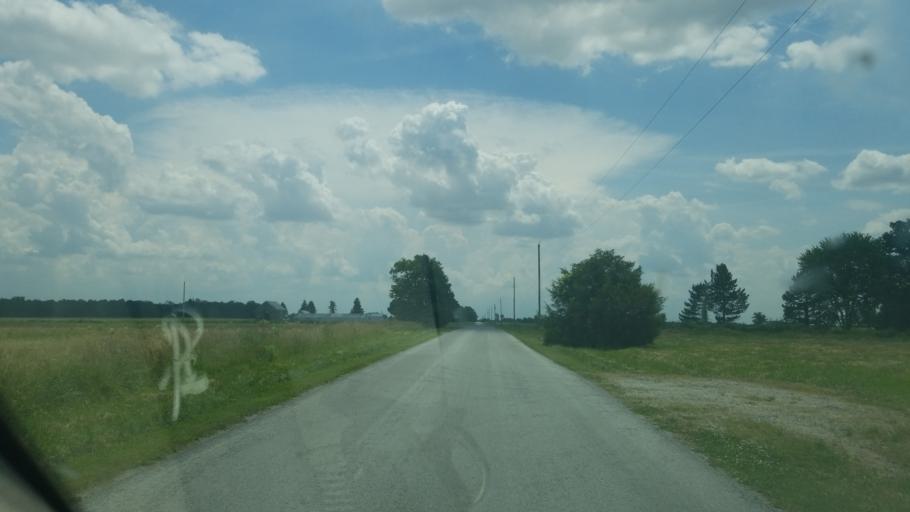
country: US
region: Ohio
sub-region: Hardin County
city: Forest
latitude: 40.8057
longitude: -83.6050
